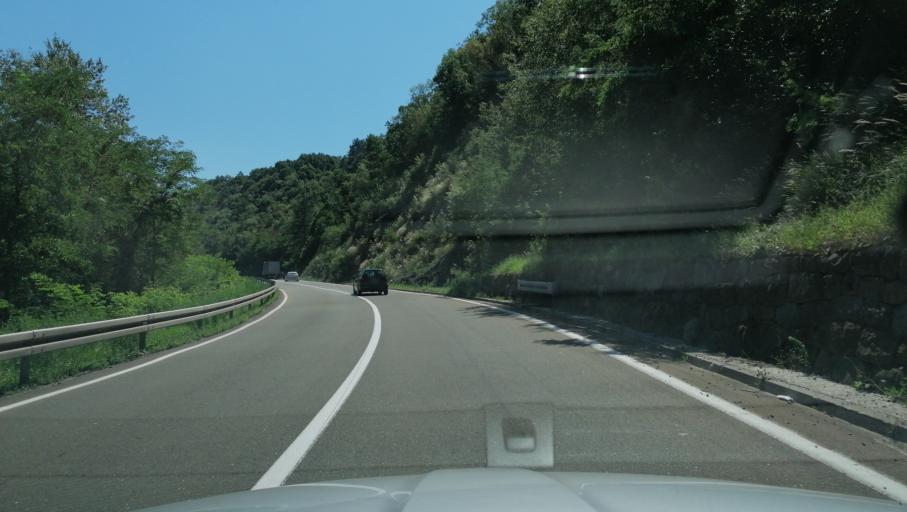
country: RS
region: Central Serbia
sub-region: Raski Okrug
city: Kraljevo
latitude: 43.5774
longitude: 20.5868
